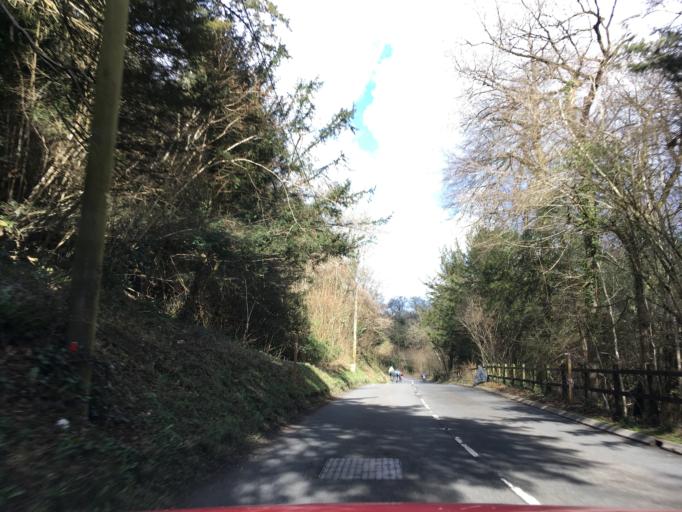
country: GB
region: Wales
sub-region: Monmouthshire
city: Tintern
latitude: 51.6813
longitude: -2.6764
